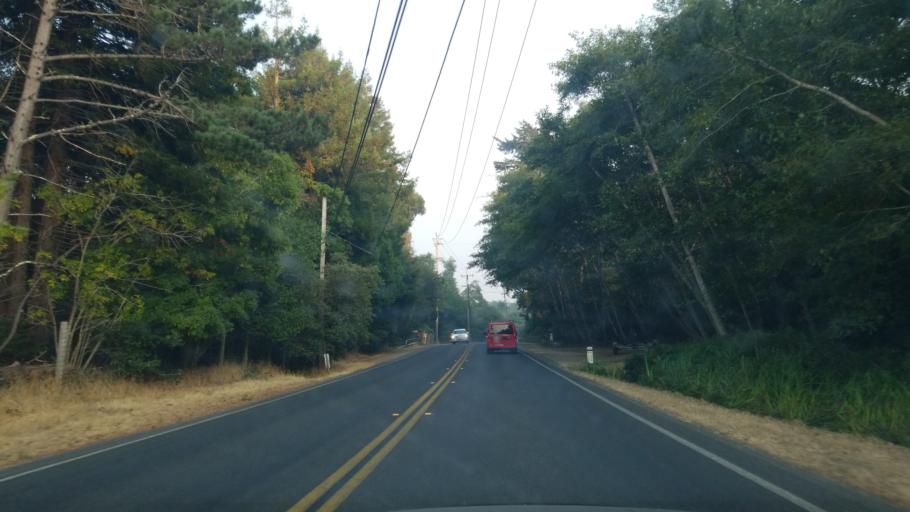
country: US
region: California
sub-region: Marin County
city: Inverness
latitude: 38.0895
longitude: -122.8435
